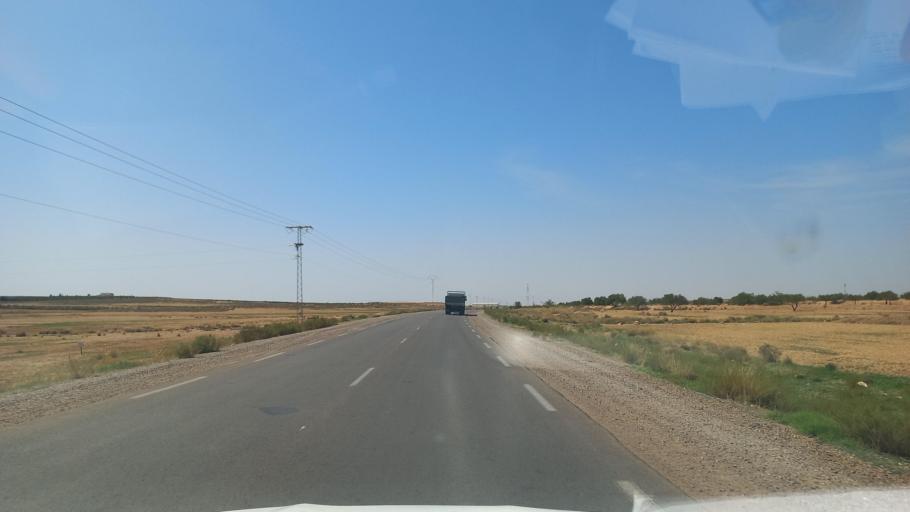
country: TN
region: Al Qasrayn
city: Sbiba
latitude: 35.3853
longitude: 9.1129
